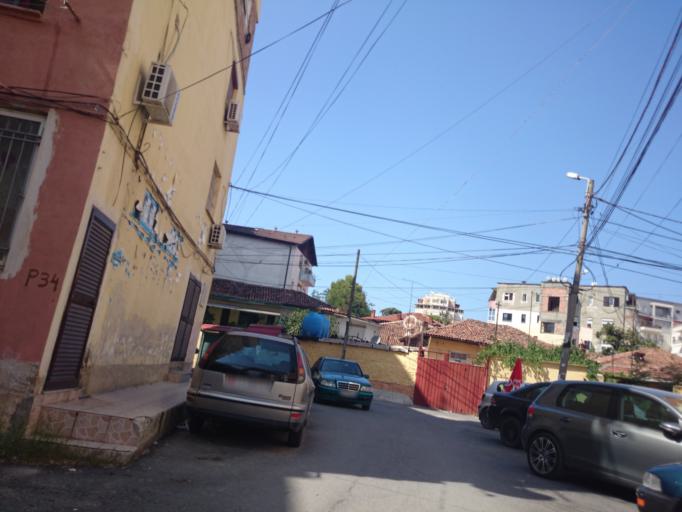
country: AL
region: Tirane
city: Tirana
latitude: 41.3282
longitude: 19.8259
